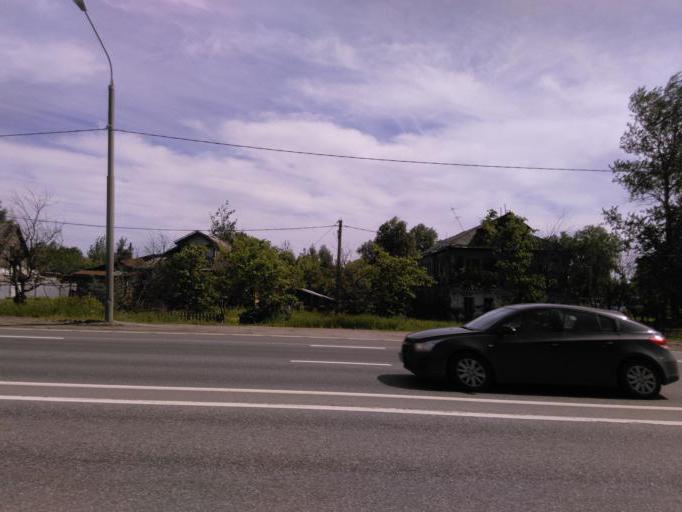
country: RU
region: Moskovskaya
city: Novopodrezkovo
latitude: 55.9339
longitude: 37.3738
